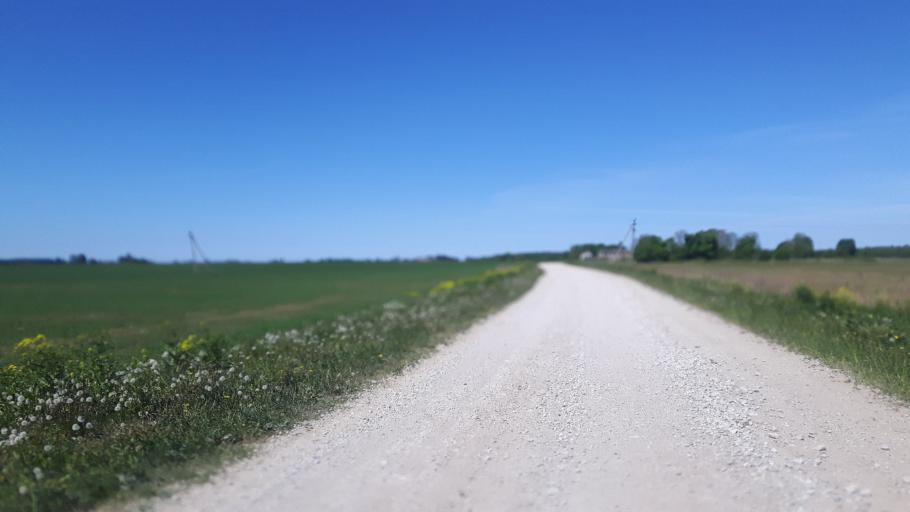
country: EE
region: Ida-Virumaa
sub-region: Toila vald
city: Voka
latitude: 59.3980
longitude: 27.6678
